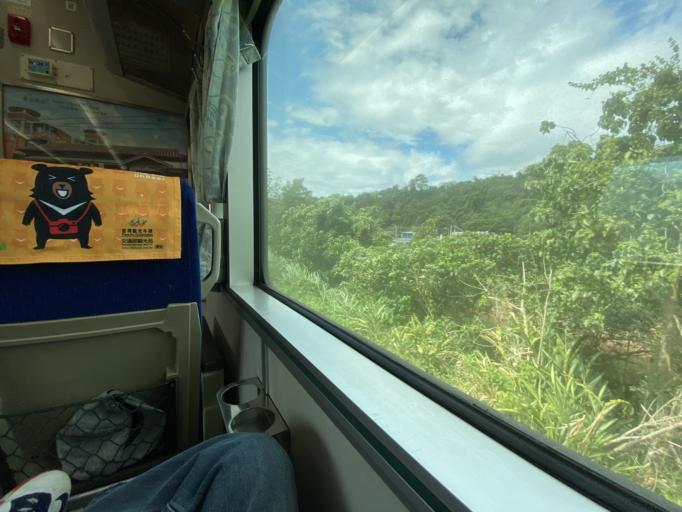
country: TW
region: Taiwan
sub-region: Taitung
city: Taitung
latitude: 22.9076
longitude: 121.1375
